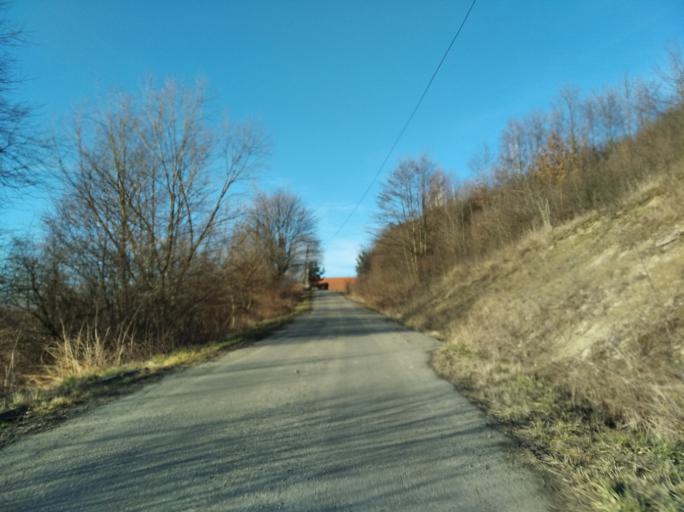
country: PL
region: Subcarpathian Voivodeship
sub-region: Powiat strzyzowski
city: Strzyzow
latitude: 49.8270
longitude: 21.8328
